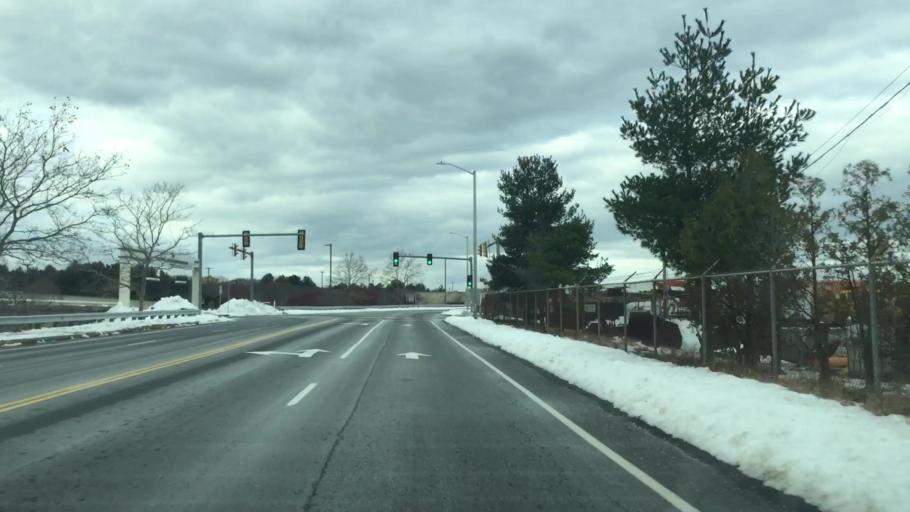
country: US
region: New Hampshire
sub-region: Rockingham County
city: Salem
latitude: 42.7695
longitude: -71.2301
